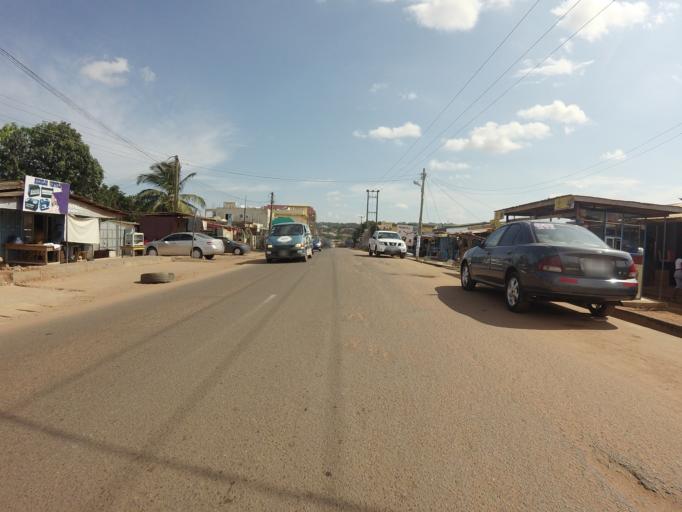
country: GH
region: Greater Accra
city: Medina Estates
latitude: 5.6769
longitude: -0.1815
